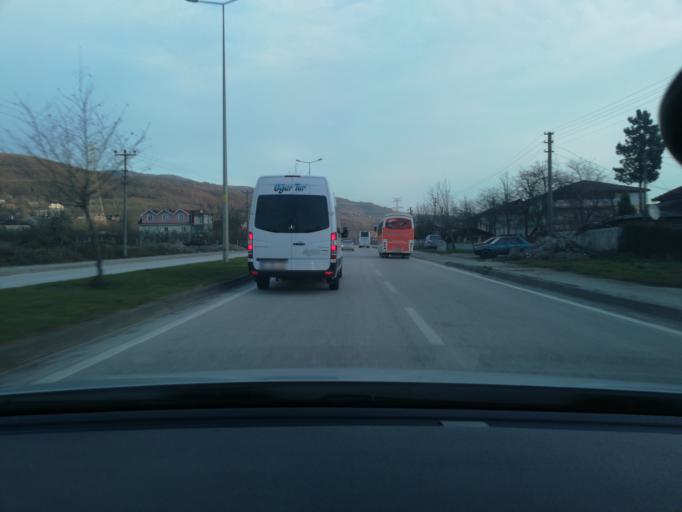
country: TR
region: Duzce
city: Konuralp
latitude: 40.9186
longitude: 31.1434
